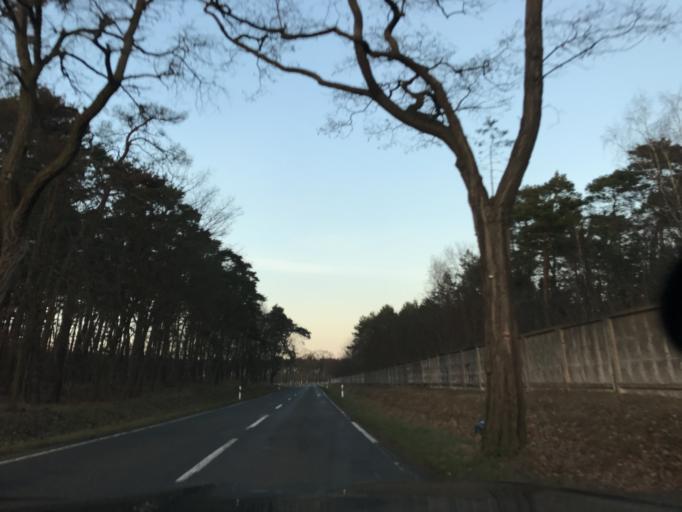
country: DE
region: Brandenburg
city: Wusterwitz
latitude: 52.4475
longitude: 12.4338
